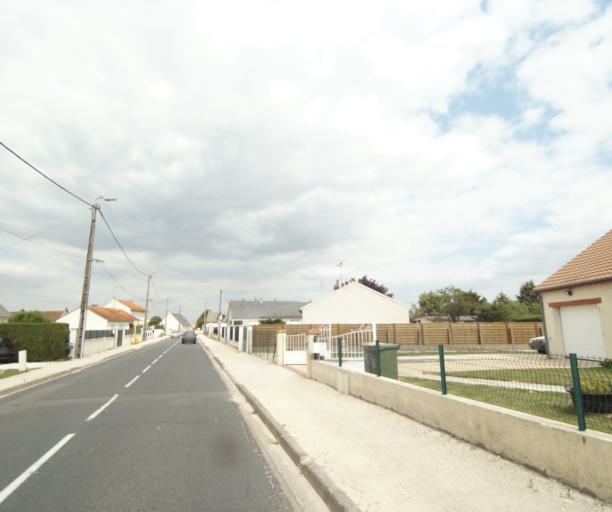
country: FR
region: Centre
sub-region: Departement du Loiret
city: Saran
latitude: 47.9339
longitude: 1.8669
